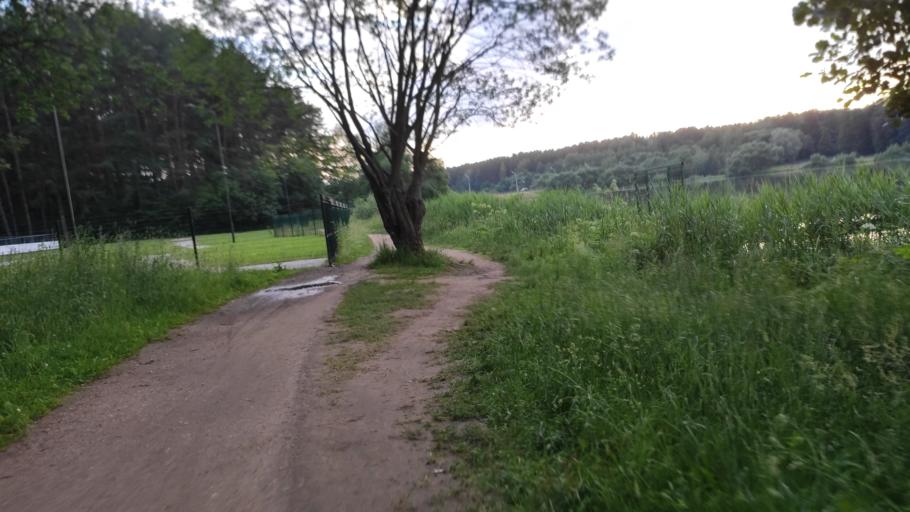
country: BY
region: Minsk
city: Zhdanovichy
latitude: 53.9629
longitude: 27.4315
